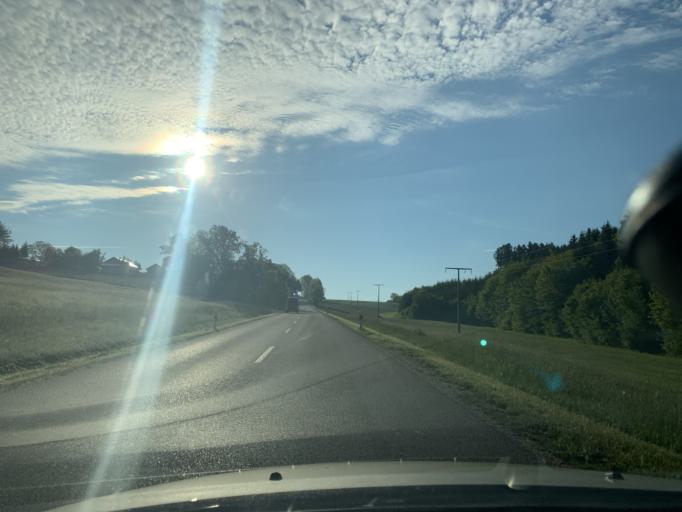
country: DE
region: Bavaria
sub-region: Lower Bavaria
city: Stallwang
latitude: 48.5322
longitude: 12.2400
